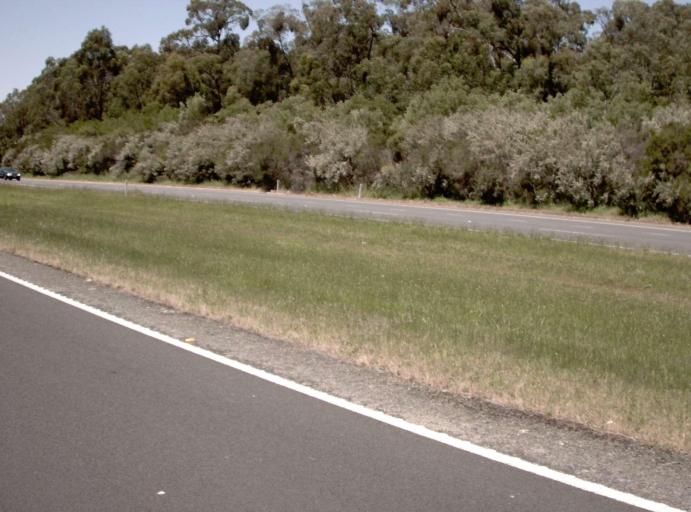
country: AU
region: Victoria
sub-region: Cardinia
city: Bunyip
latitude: -38.0946
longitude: 145.8311
